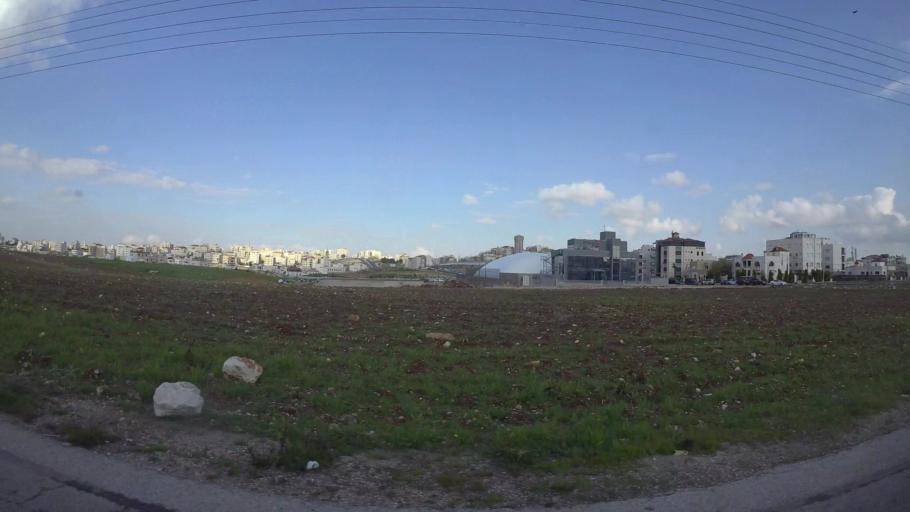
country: JO
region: Amman
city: Al Bunayyat ash Shamaliyah
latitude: 31.9113
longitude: 35.8776
